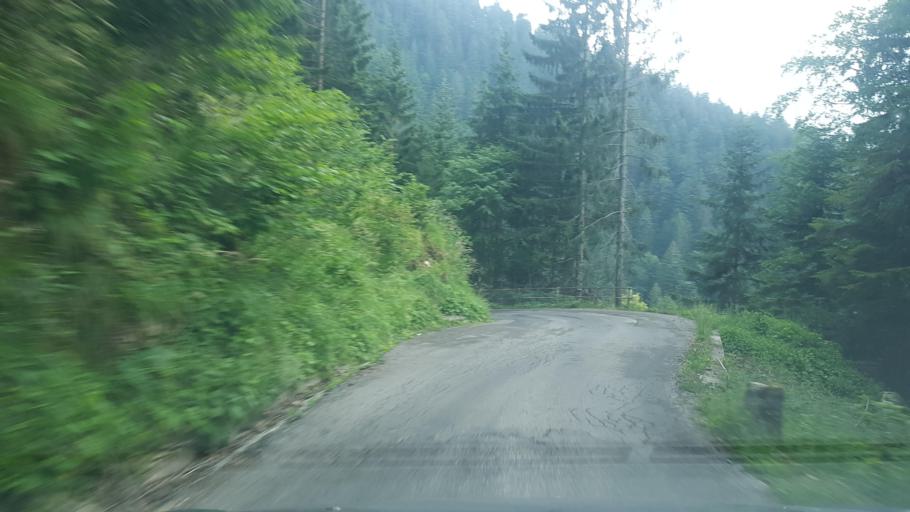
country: IT
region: Friuli Venezia Giulia
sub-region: Provincia di Udine
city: Paularo
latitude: 46.5580
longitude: 13.1259
